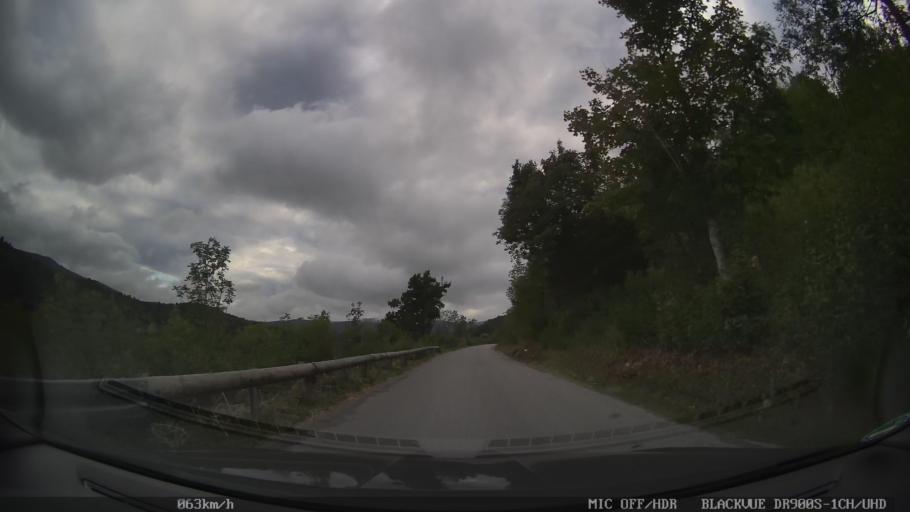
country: HR
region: Licko-Senjska
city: Jezerce
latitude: 44.9296
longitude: 15.6210
